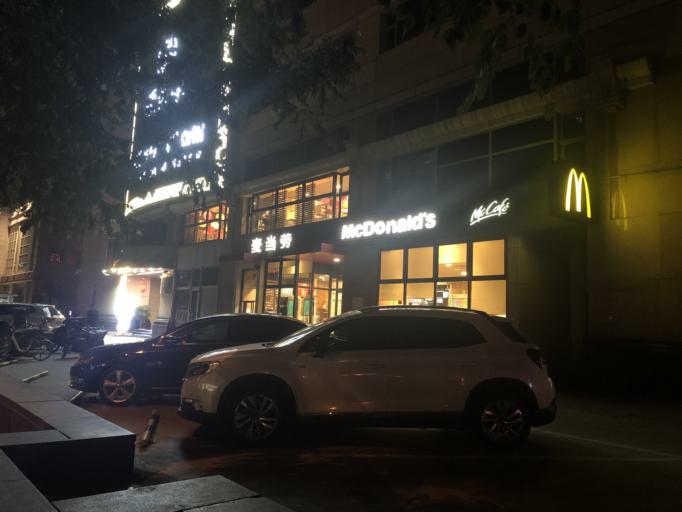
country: CN
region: Beijing
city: Datun
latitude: 40.0035
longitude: 116.4013
